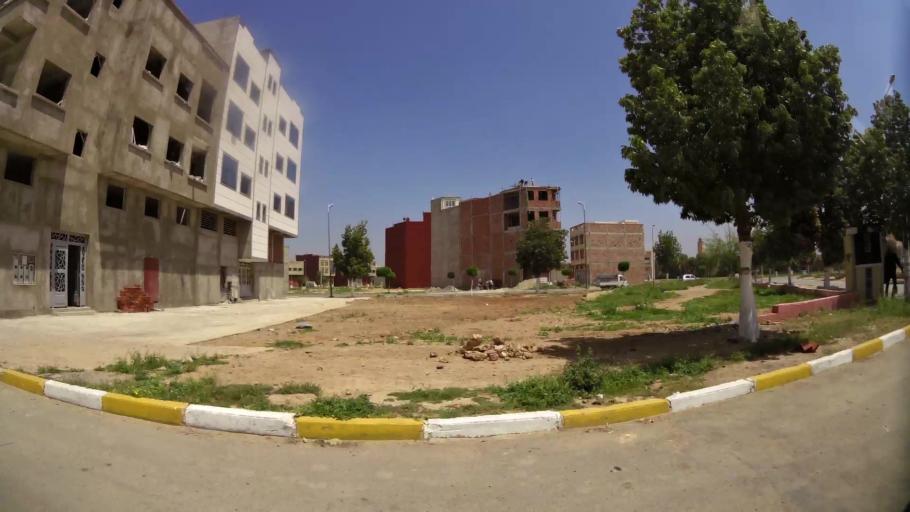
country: MA
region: Oriental
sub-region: Oujda-Angad
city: Oujda
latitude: 34.6920
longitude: -1.8926
